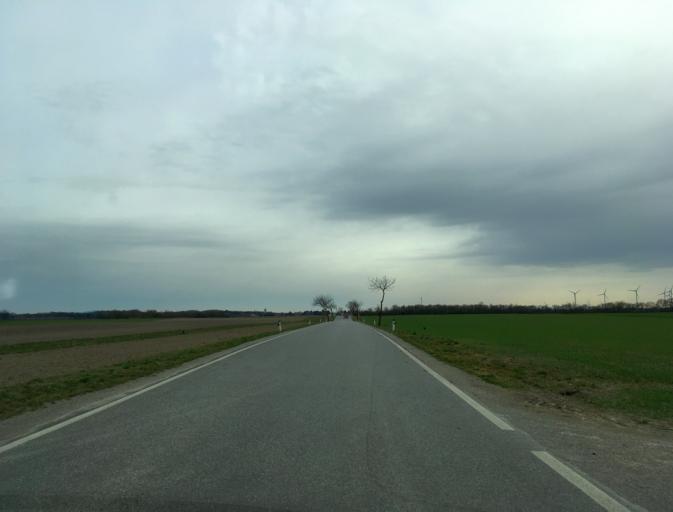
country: AT
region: Lower Austria
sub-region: Politischer Bezirk Ganserndorf
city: Leopoldsdorf im Marchfelde
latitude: 48.2387
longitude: 16.6705
